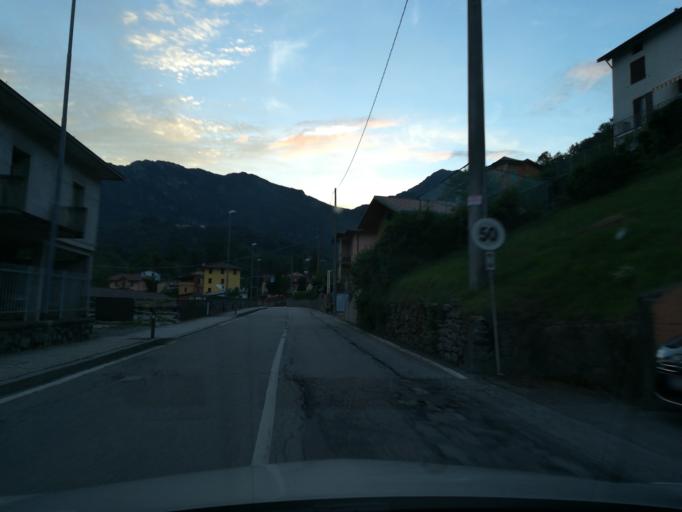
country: IT
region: Lombardy
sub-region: Provincia di Bergamo
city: Rota d'Imagna
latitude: 45.8193
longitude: 9.5180
